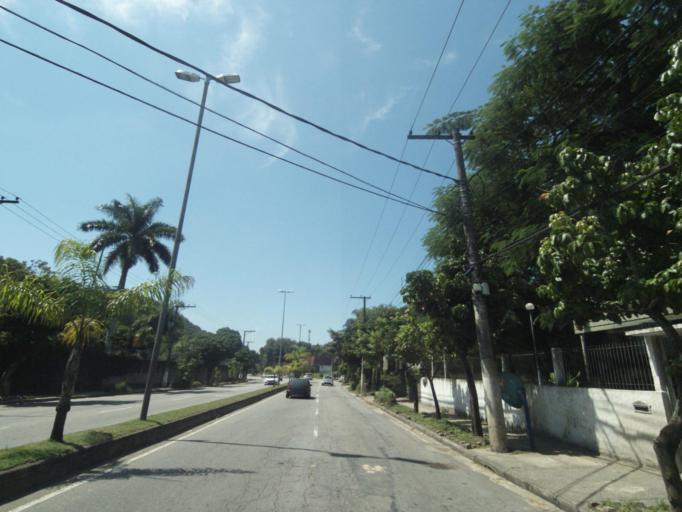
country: BR
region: Rio de Janeiro
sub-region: Niteroi
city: Niteroi
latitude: -22.8970
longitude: -43.0394
